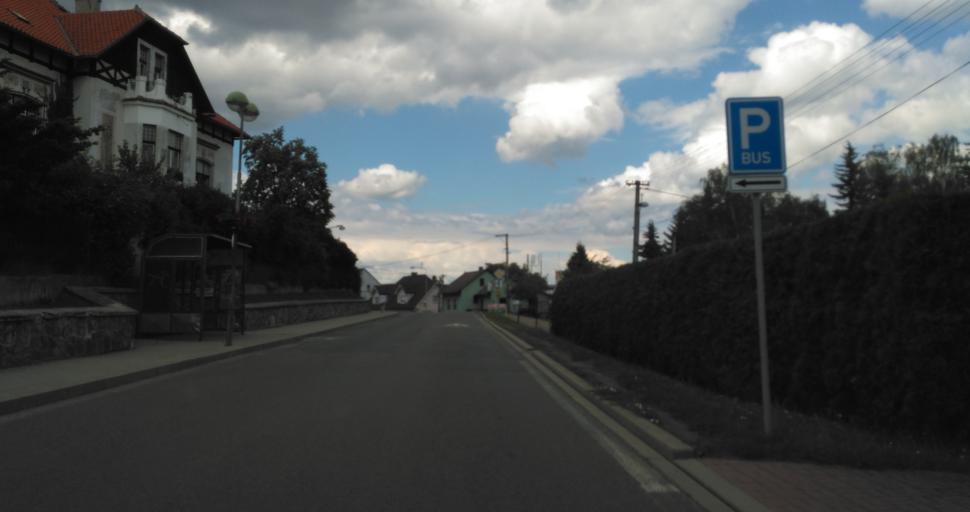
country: CZ
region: Plzensky
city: Zbiroh
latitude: 49.8556
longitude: 13.7691
